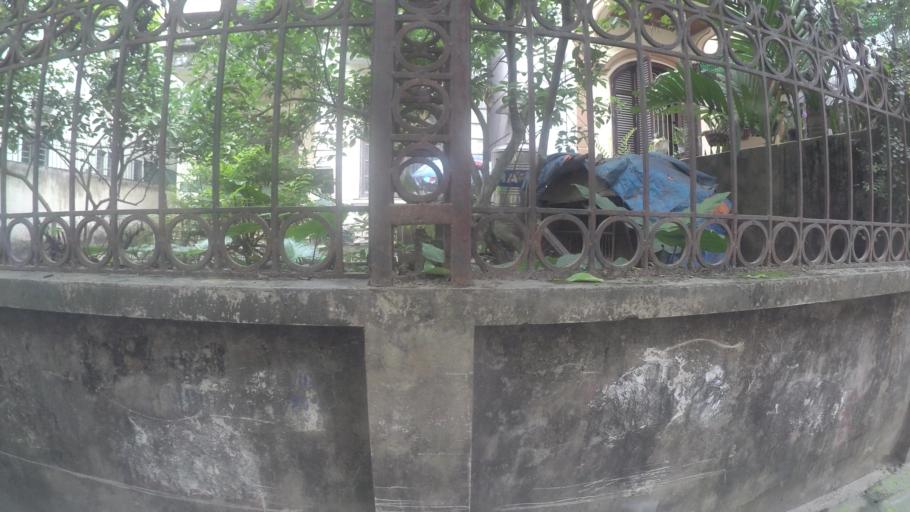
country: VN
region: Ha Noi
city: Tay Ho
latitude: 21.0630
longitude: 105.8339
